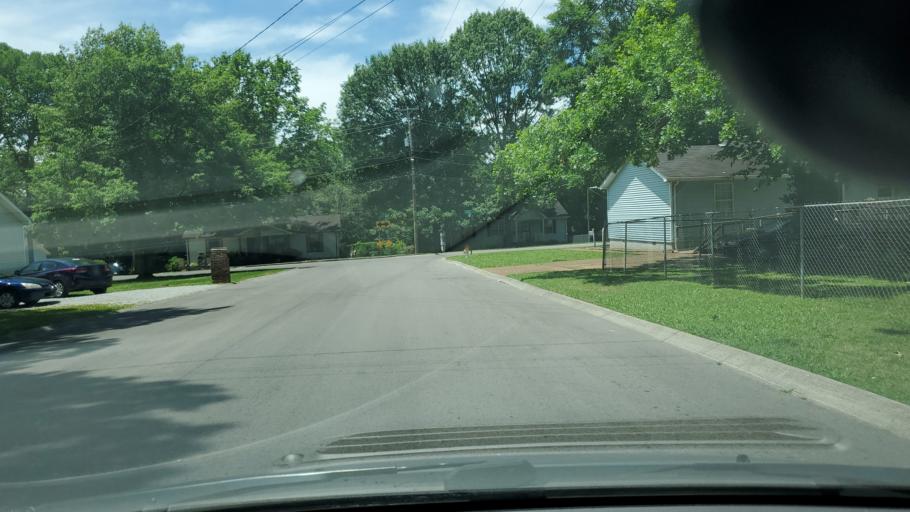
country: US
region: Tennessee
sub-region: Davidson County
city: Nashville
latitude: 36.2159
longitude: -86.7574
